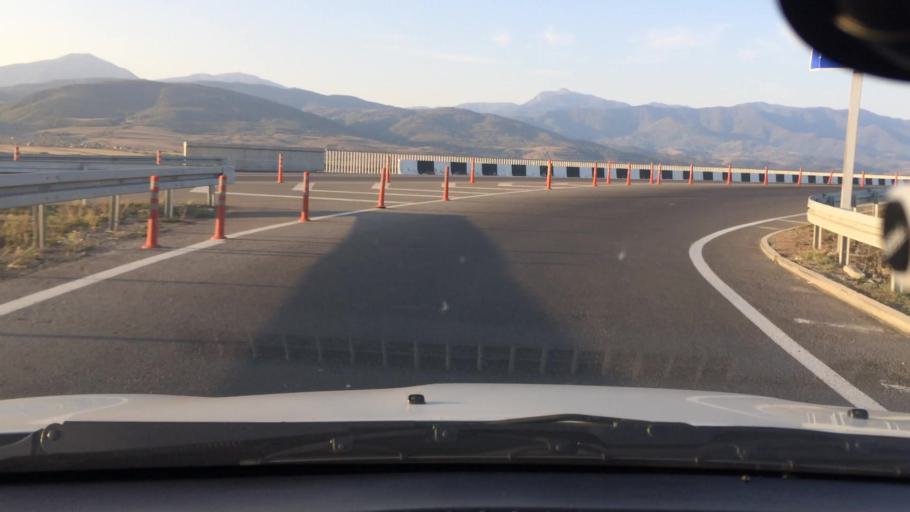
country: GE
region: Shida Kartli
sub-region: Khashuris Raioni
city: Khashuri
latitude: 42.0118
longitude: 43.7004
